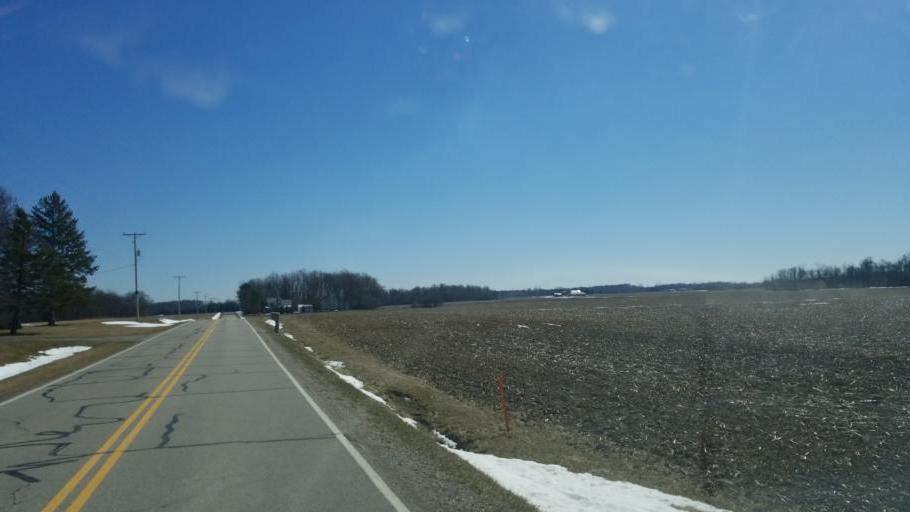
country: US
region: Ohio
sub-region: Crawford County
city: Bucyrus
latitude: 40.8048
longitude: -83.0429
